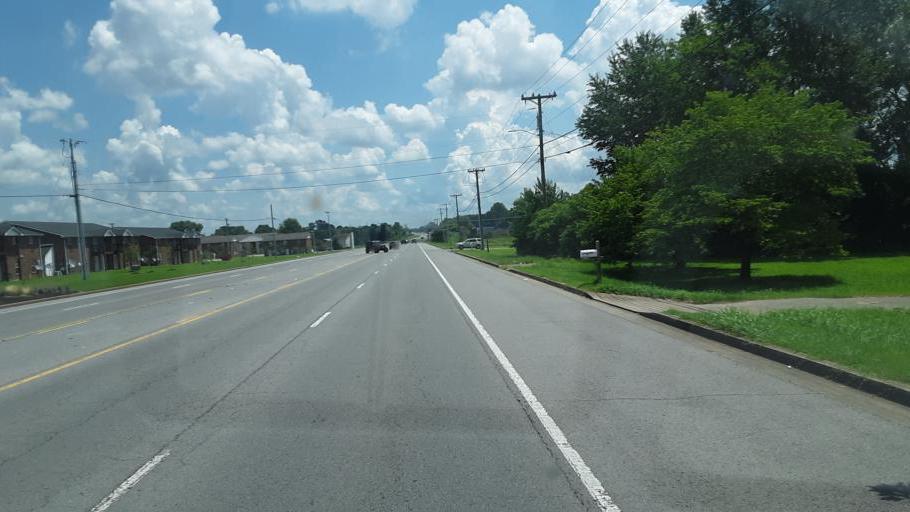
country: US
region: Kentucky
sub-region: Christian County
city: Oak Grove
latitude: 36.6323
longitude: -87.4126
